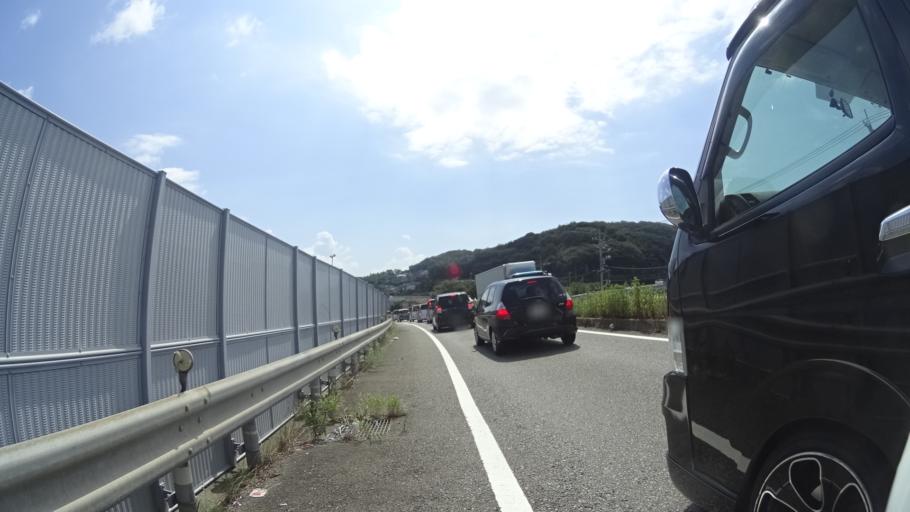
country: JP
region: Yamaguchi
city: Shimonoseki
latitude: 33.9785
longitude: 130.9467
